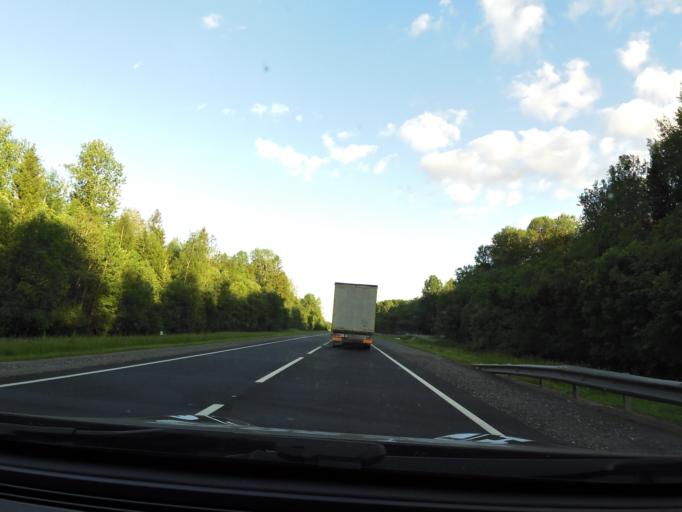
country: RU
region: Vologda
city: Gryazovets
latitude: 58.9683
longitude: 40.1557
